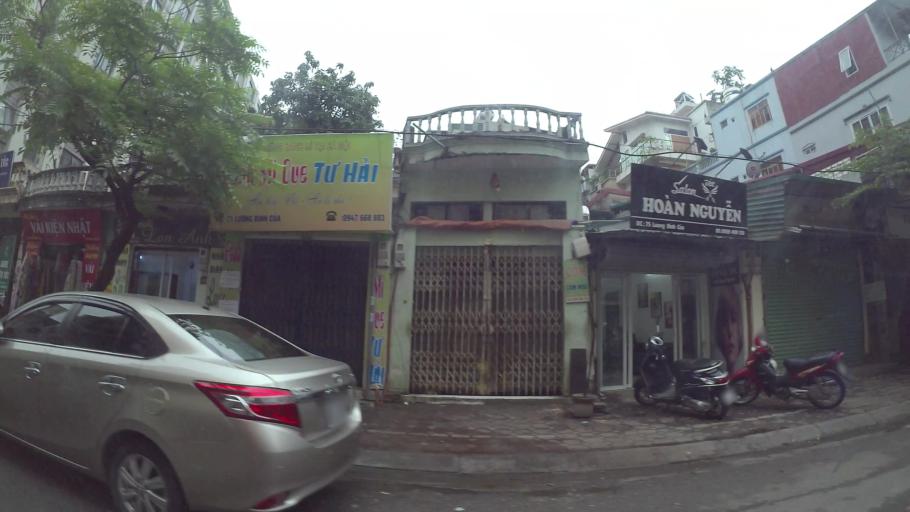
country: VN
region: Ha Noi
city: Hai BaTrung
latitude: 21.0031
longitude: 105.8360
